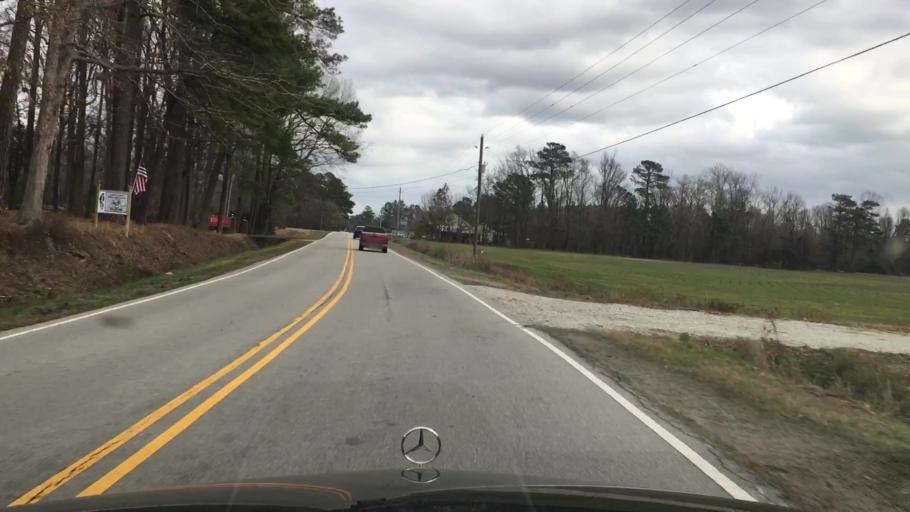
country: US
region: North Carolina
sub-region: Onslow County
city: Richlands
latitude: 34.8782
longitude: -77.5163
